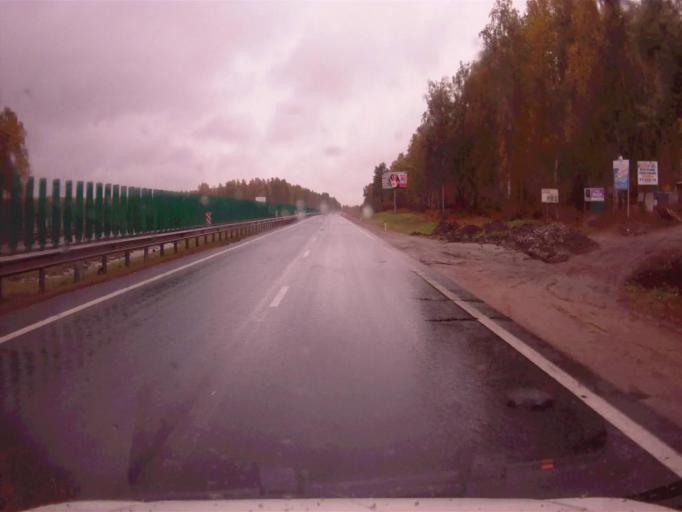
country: RU
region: Chelyabinsk
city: Dolgoderevenskoye
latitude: 55.3315
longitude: 61.3187
